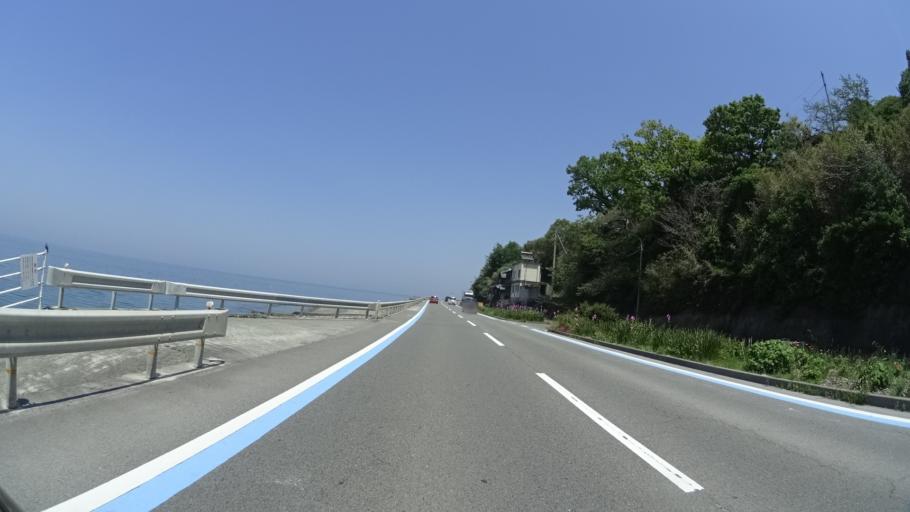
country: JP
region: Ehime
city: Iyo
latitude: 33.7039
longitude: 132.6597
